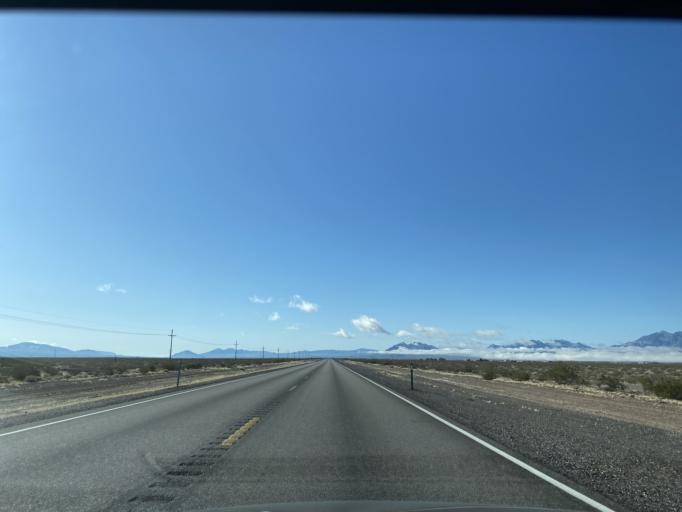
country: US
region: Nevada
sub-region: Nye County
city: Beatty
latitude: 36.5822
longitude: -116.4113
